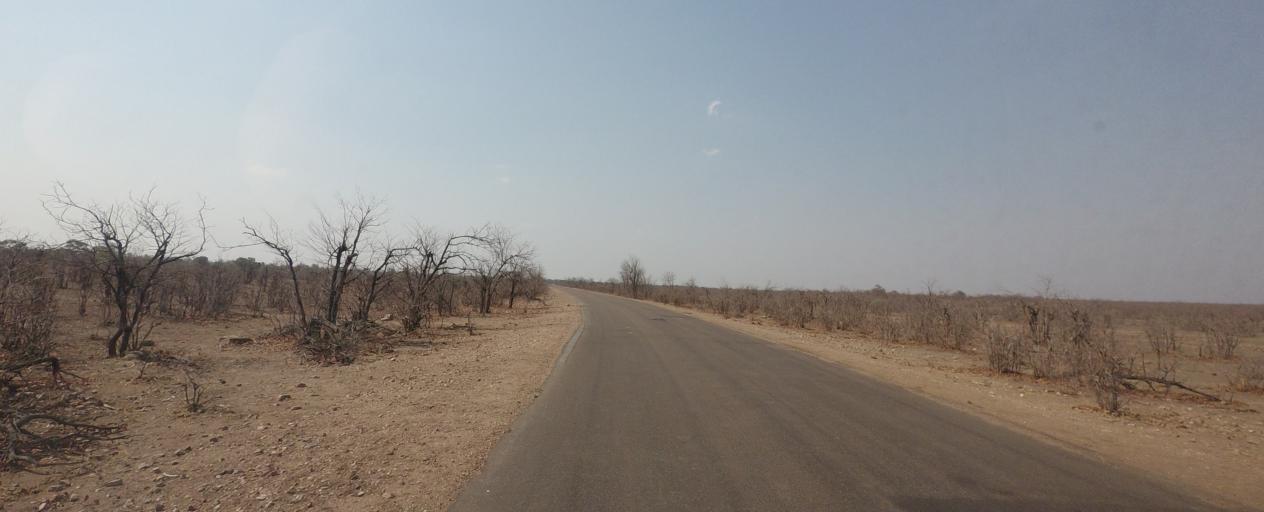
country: ZA
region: Limpopo
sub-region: Mopani District Municipality
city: Giyani
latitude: -23.1632
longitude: 31.3482
